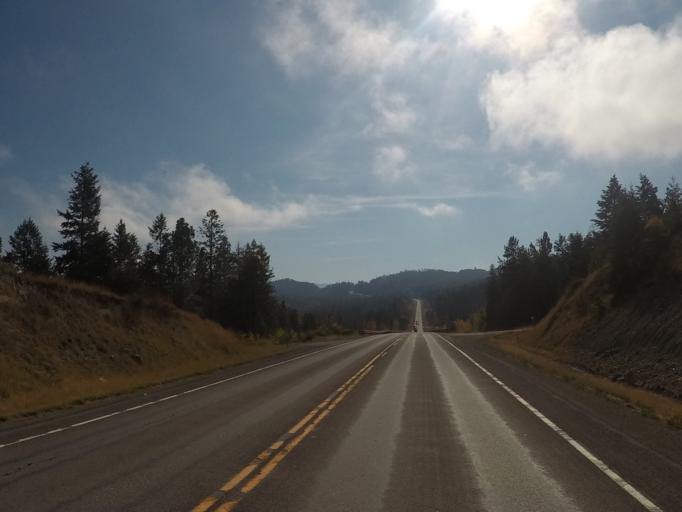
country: US
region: Montana
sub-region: Flathead County
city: Lakeside
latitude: 48.0063
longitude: -114.2186
